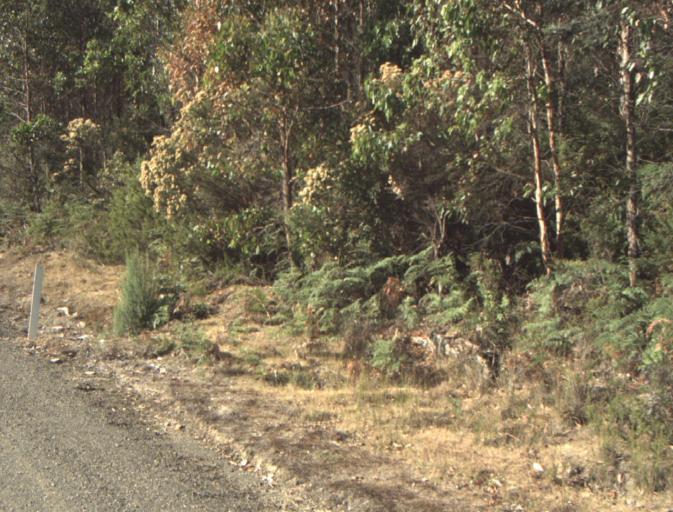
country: AU
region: Tasmania
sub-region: Dorset
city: Scottsdale
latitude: -41.2910
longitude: 147.3455
